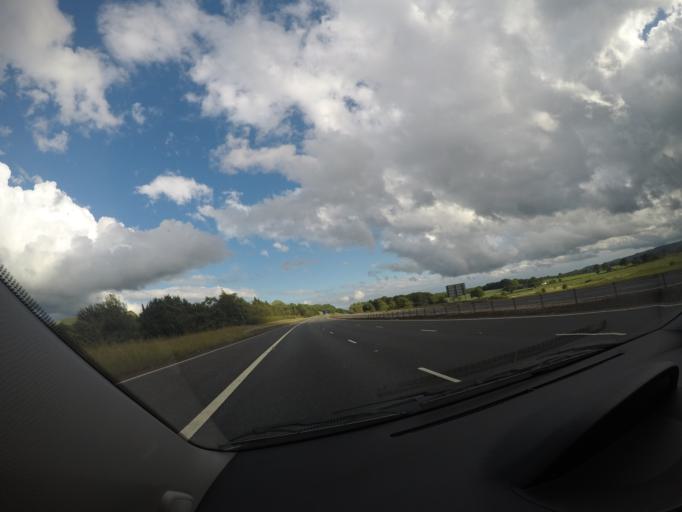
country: GB
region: Scotland
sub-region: Dumfries and Galloway
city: Lockerbie
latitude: 55.1424
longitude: -3.3743
